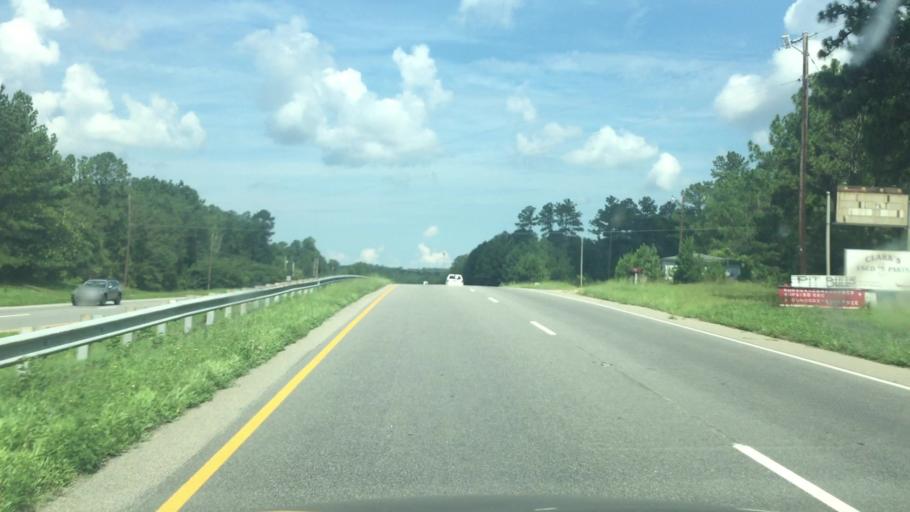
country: US
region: North Carolina
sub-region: Richmond County
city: Hamlet
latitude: 34.8625
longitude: -79.6346
